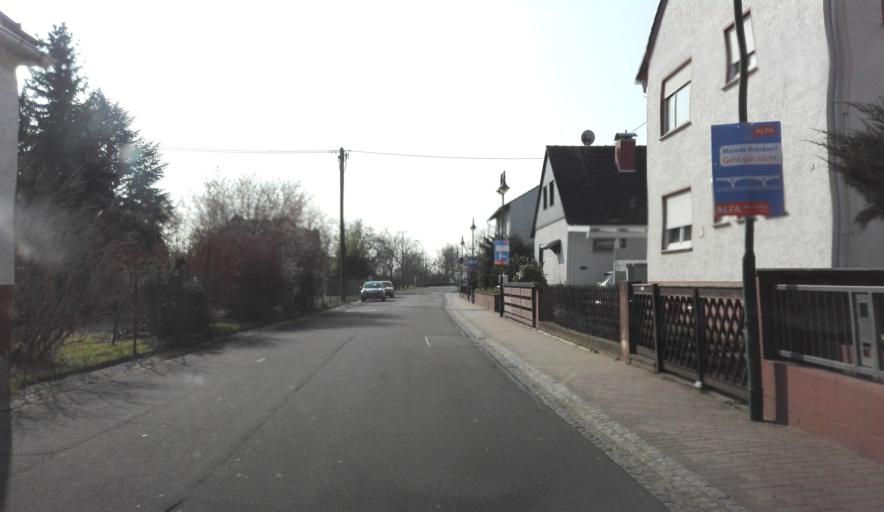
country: DE
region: Rheinland-Pfalz
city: Heuchelheim bei Frankenthal
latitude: 49.5614
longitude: 8.2897
